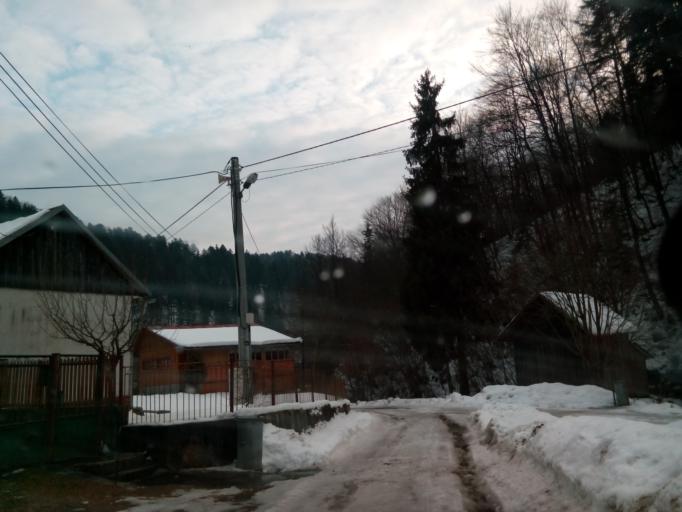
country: SK
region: Presovsky
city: Sabinov
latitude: 49.1947
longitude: 21.0899
